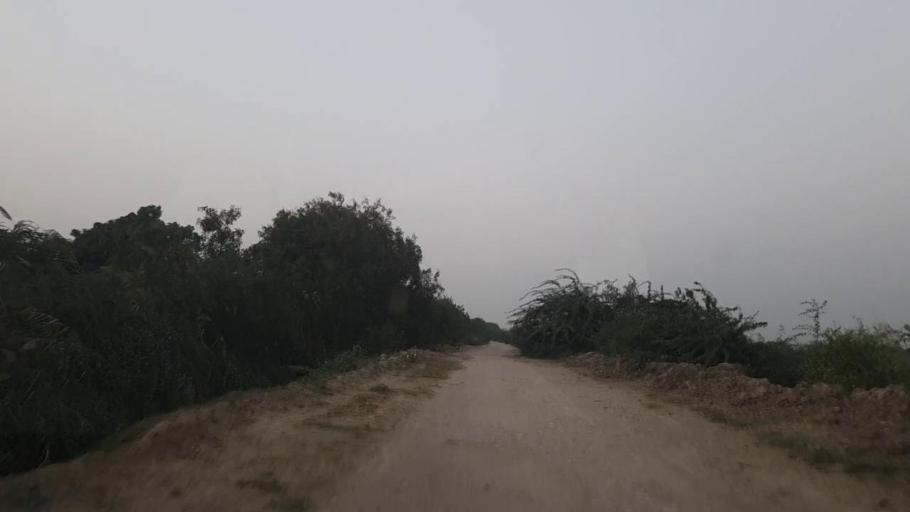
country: PK
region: Sindh
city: Mirpur Sakro
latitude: 24.5804
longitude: 67.7853
